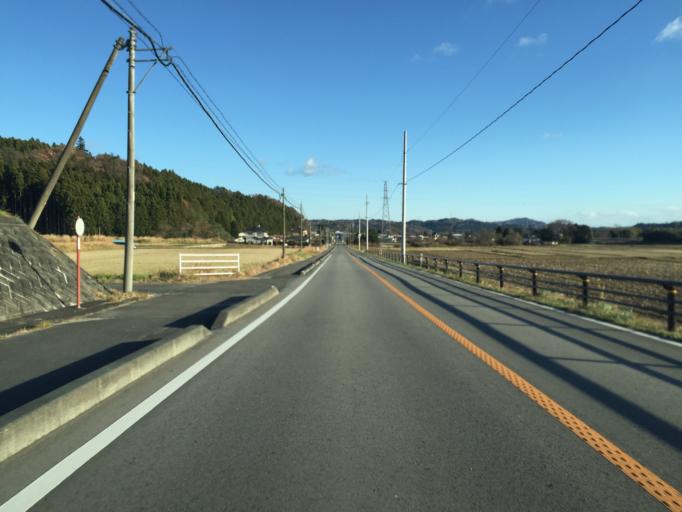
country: JP
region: Fukushima
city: Iwaki
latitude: 37.1395
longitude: 140.8462
